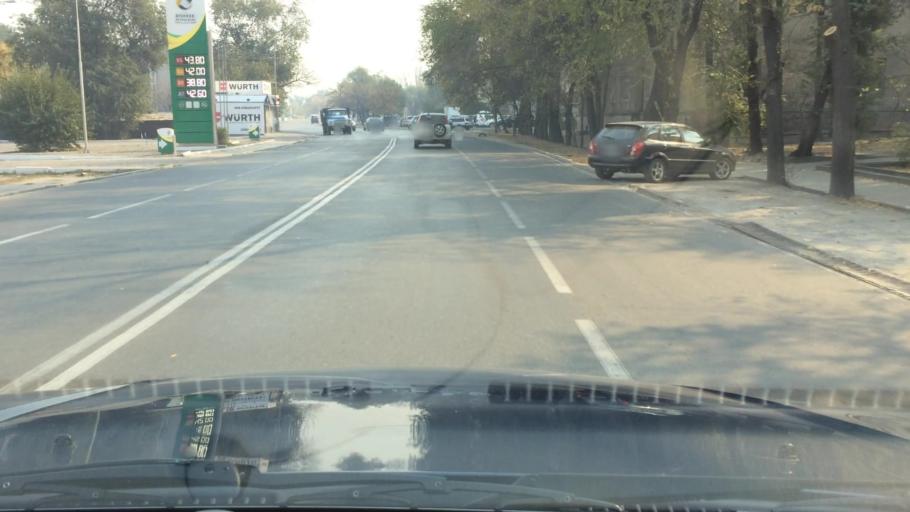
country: KG
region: Chuy
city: Bishkek
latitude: 42.8626
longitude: 74.6073
